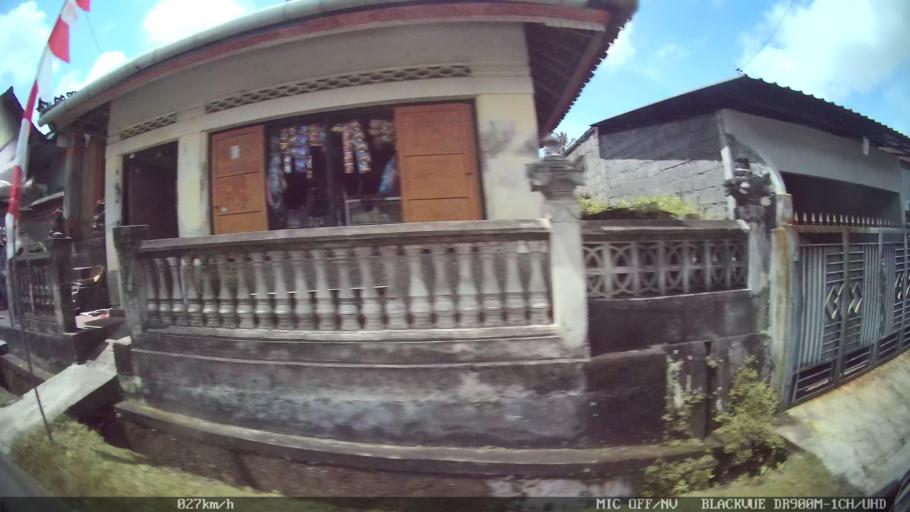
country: ID
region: Bali
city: Banjar Kelodan
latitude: -8.5170
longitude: 115.3754
